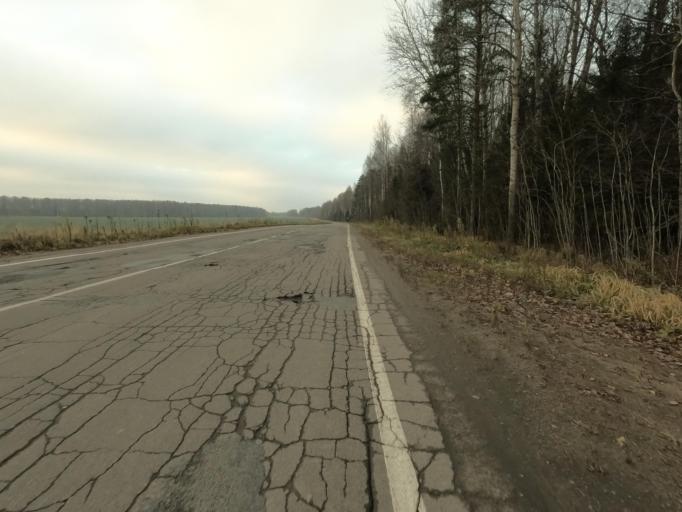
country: RU
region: Leningrad
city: Mga
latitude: 59.7957
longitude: 31.0044
